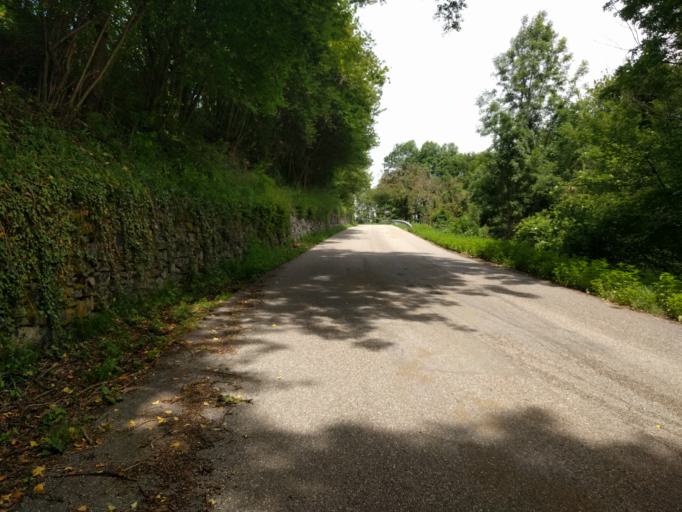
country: FR
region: Rhone-Alpes
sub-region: Departement de la Savoie
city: Saint-Remy-de-Maurienne
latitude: 45.3809
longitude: 6.2709
